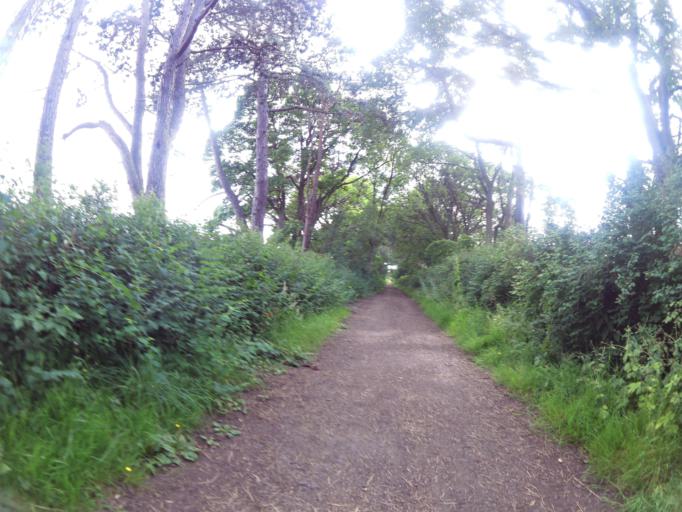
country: GB
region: Scotland
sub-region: Edinburgh
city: Kirkliston
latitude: 55.9621
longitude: -3.3839
